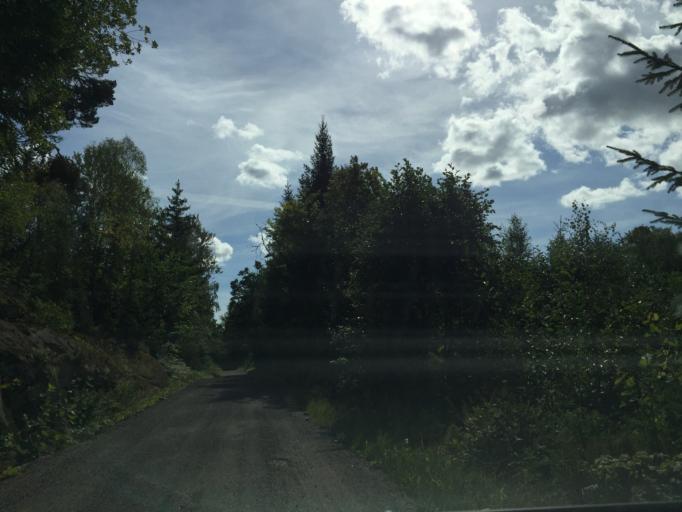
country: NO
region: Vestfold
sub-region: Hof
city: Hof
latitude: 59.4432
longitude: 10.1581
